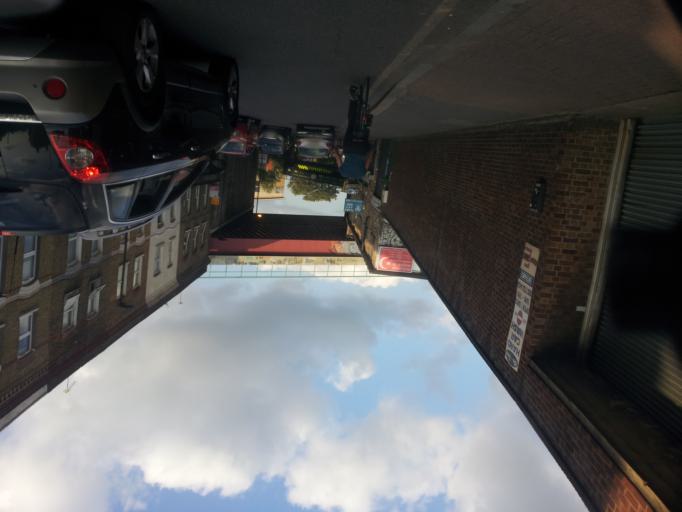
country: GB
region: England
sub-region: Greater London
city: Brixton
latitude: 51.4655
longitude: -0.1026
